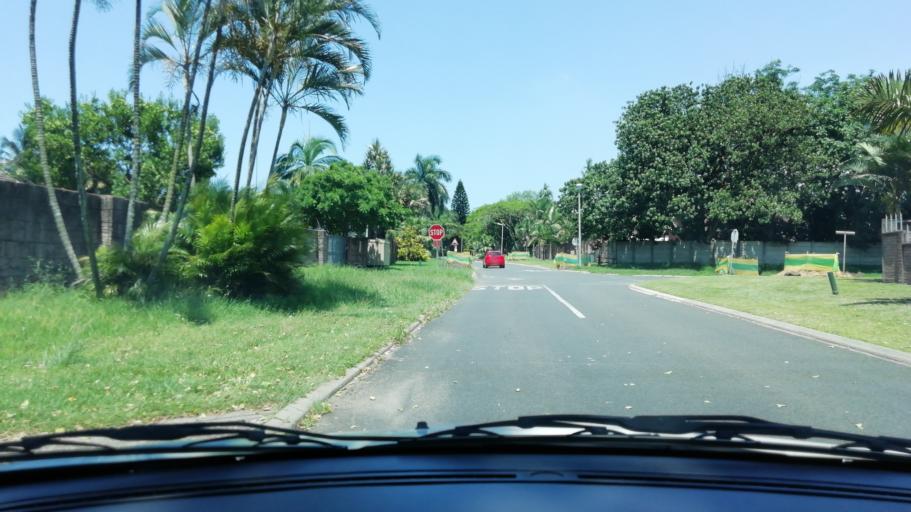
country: ZA
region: KwaZulu-Natal
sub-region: uThungulu District Municipality
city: Richards Bay
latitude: -28.7370
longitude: 32.0541
